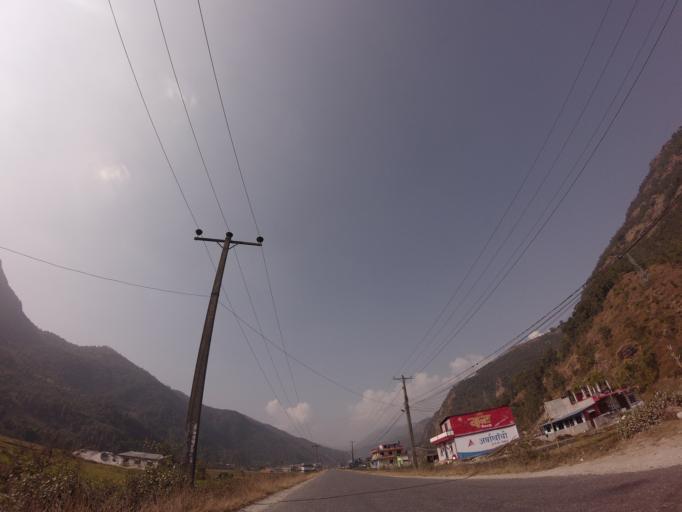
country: NP
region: Western Region
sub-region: Gandaki Zone
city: Pokhara
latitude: 28.2850
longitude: 83.9092
